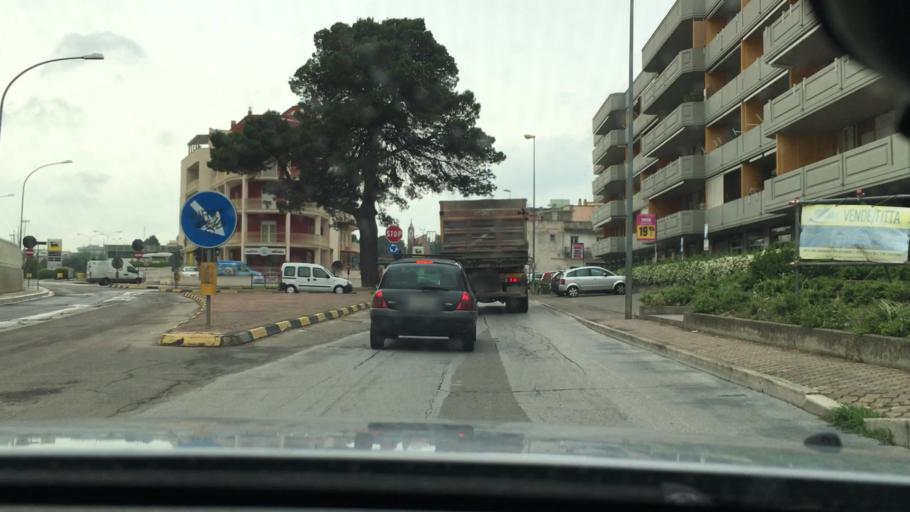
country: IT
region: Apulia
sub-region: Provincia di Bari
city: Gioia del Colle
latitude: 40.8072
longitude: 16.9244
